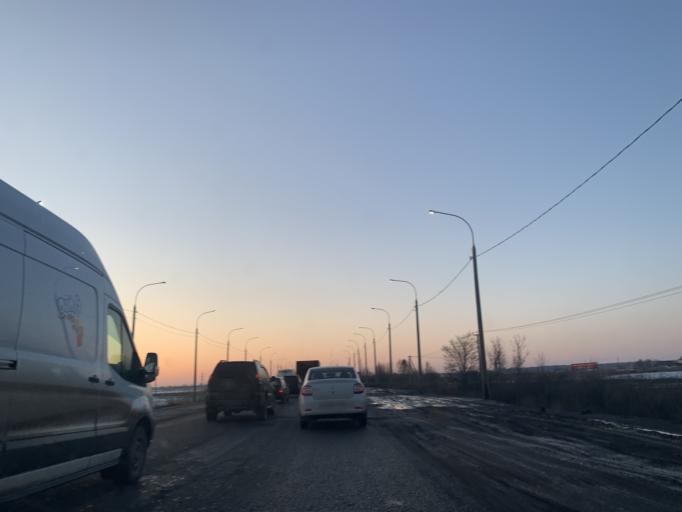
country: RU
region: Jaroslavl
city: Yaroslavl
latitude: 57.6252
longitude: 39.7649
